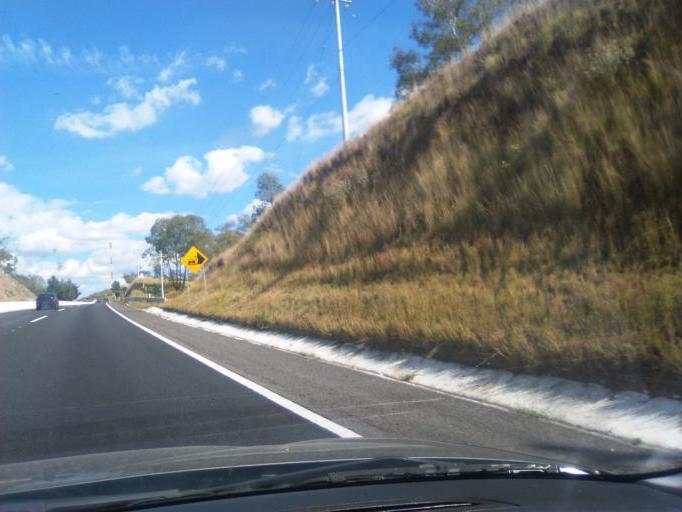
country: MX
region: Guanajuato
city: Santa Teresa
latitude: 20.9642
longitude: -101.3343
